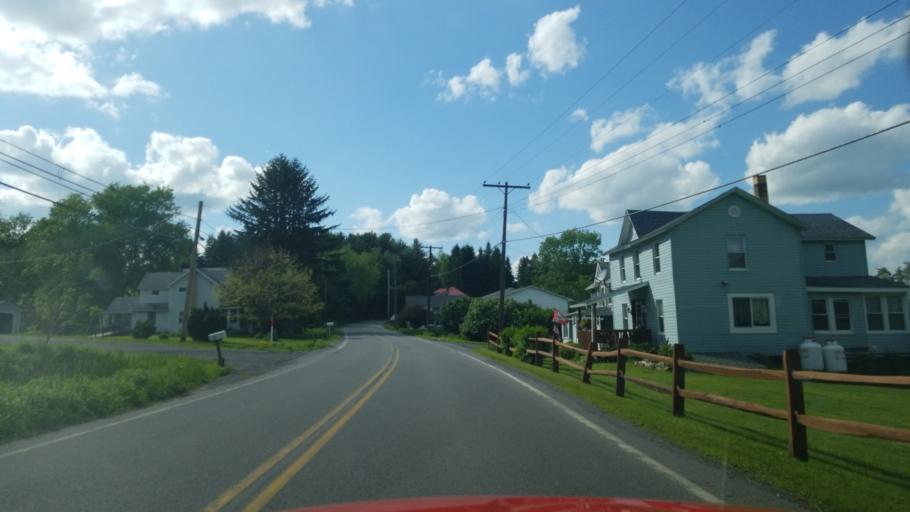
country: US
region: Pennsylvania
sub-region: Centre County
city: Philipsburg
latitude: 40.9091
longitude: -78.2452
